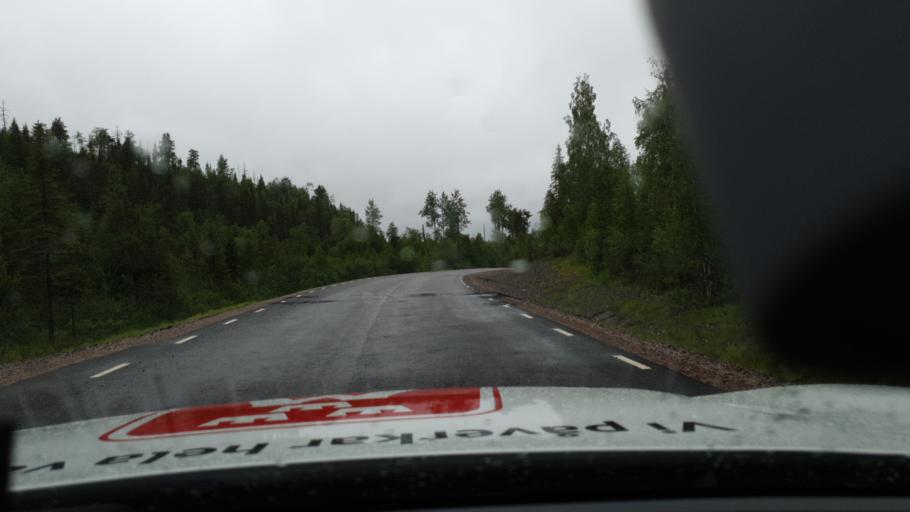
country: SE
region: Norrbotten
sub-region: Overtornea Kommun
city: OEvertornea
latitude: 66.5237
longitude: 23.3726
